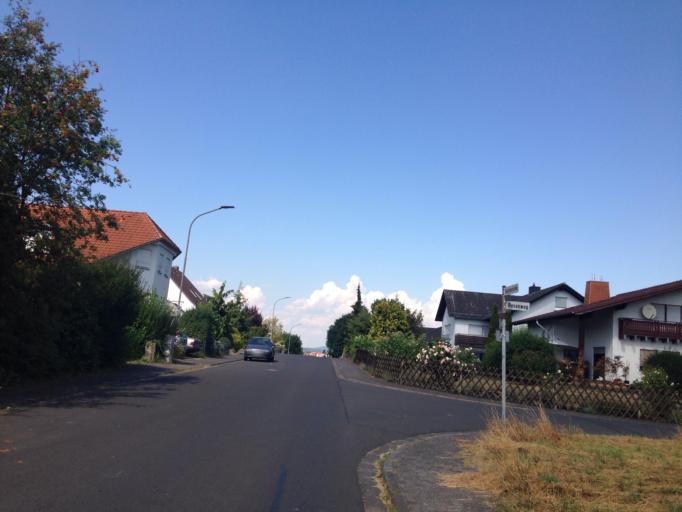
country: DE
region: Hesse
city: Allendorf an der Lahn
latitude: 50.5423
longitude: 8.6256
